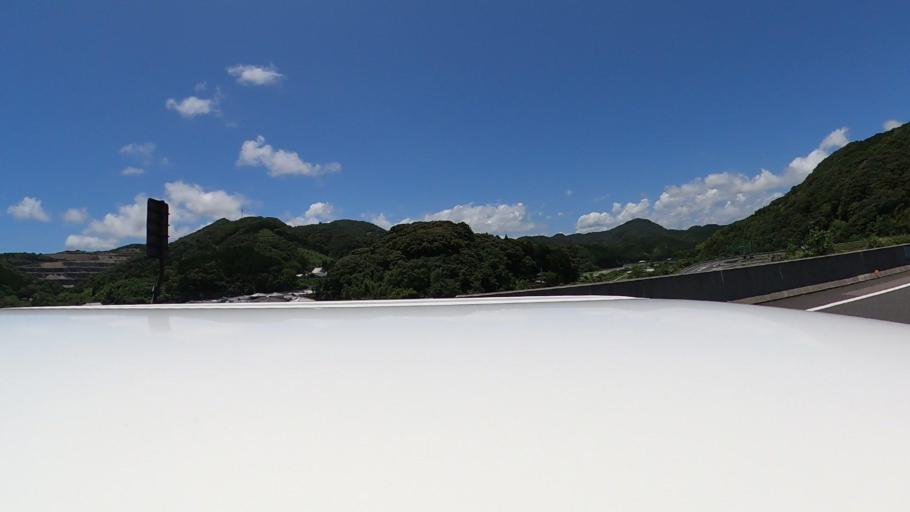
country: JP
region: Miyazaki
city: Nobeoka
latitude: 32.3996
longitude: 131.6173
